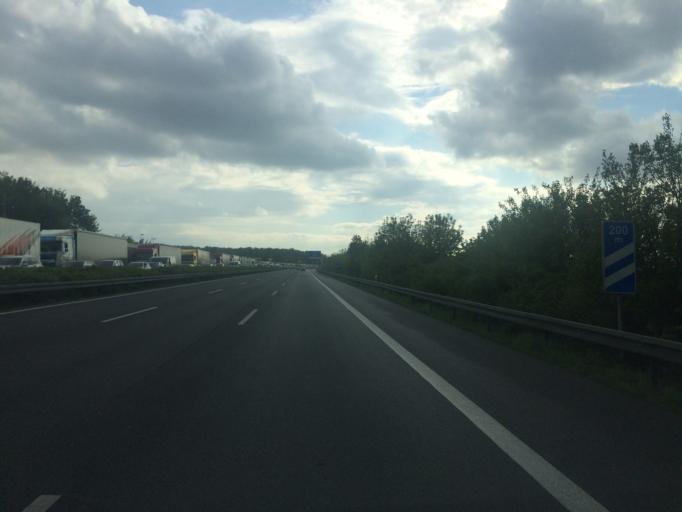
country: DE
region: Lower Saxony
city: Rehren
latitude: 52.2270
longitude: 9.2309
